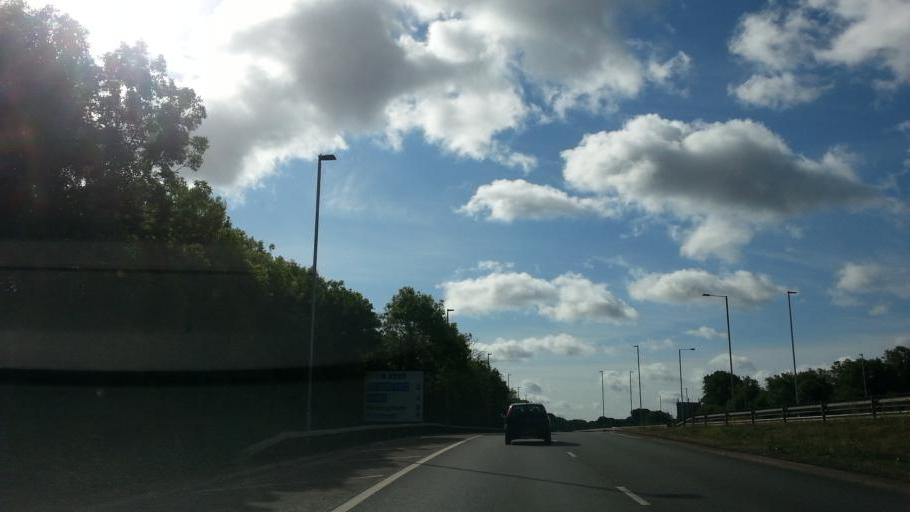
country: GB
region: England
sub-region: Wokingham
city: Earley
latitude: 51.4539
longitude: -0.9359
